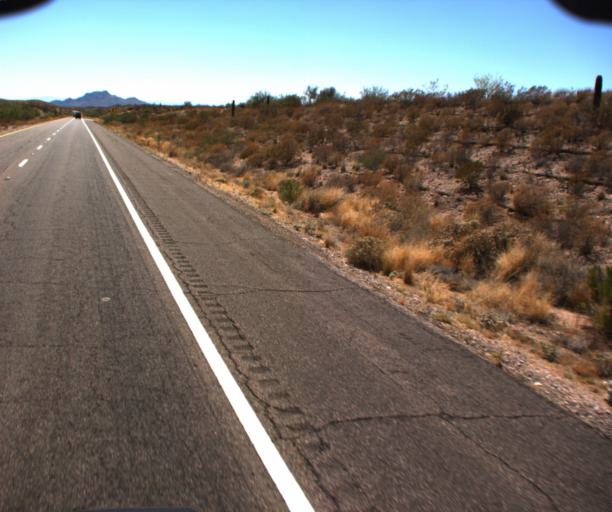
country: US
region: Arizona
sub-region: Maricopa County
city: Rio Verde
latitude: 33.6277
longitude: -111.5597
